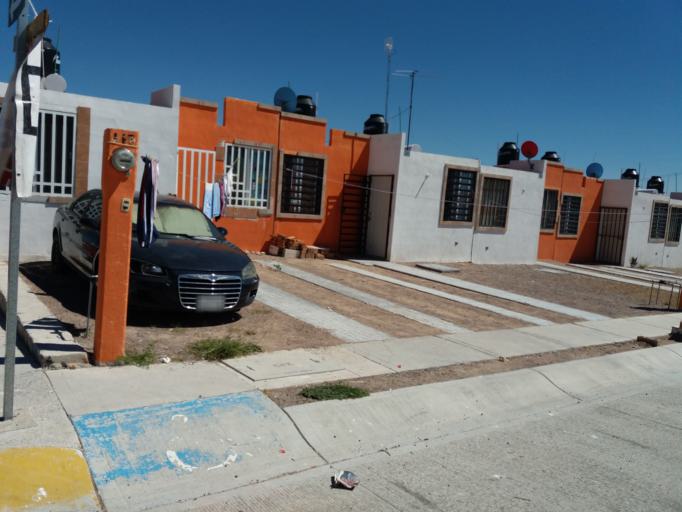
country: MX
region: Aguascalientes
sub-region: Aguascalientes
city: Cumbres III
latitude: 21.8717
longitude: -102.2295
